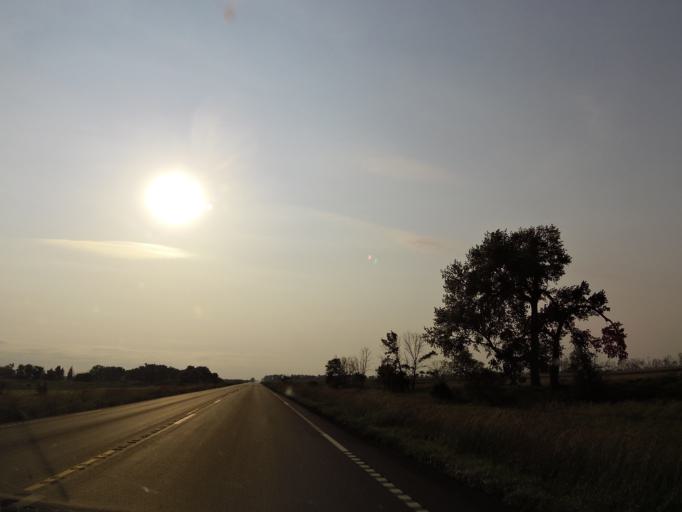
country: US
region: North Dakota
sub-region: Traill County
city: Mayville
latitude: 47.3529
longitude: -97.2797
